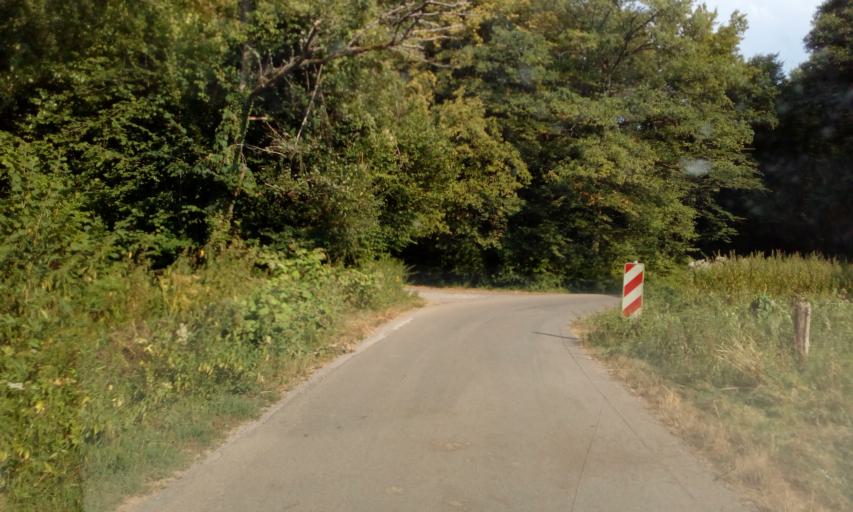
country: BE
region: Wallonia
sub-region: Province du Luxembourg
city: Tellin
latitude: 50.1106
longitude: 5.2060
